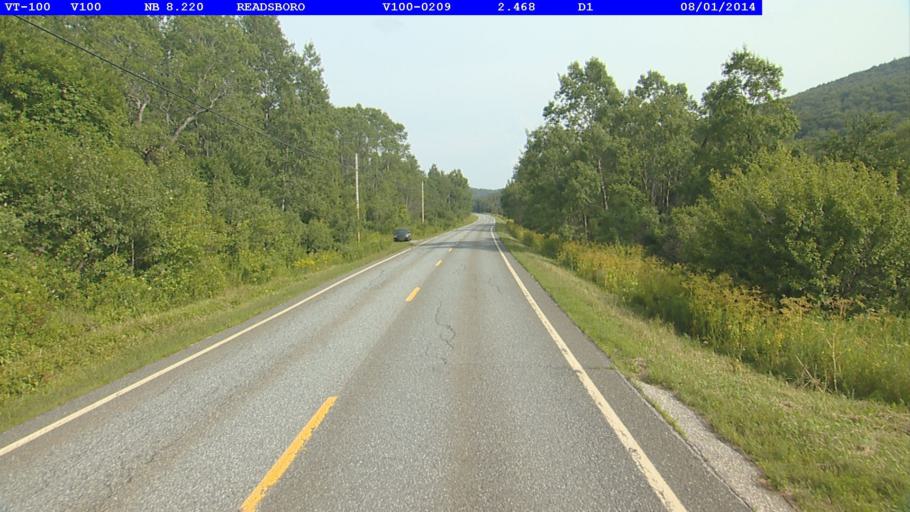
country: US
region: Massachusetts
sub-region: Berkshire County
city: North Adams
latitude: 42.8257
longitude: -72.9846
